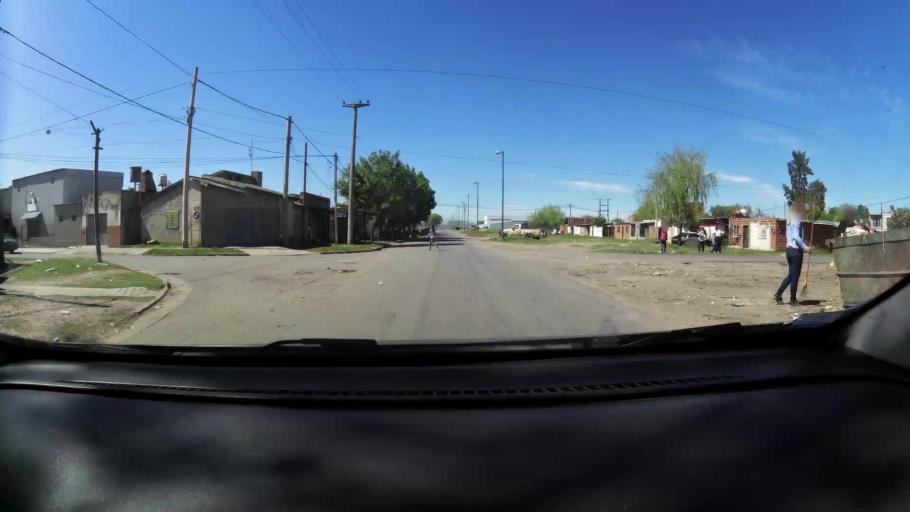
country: AR
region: Santa Fe
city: Perez
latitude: -32.9722
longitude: -60.7113
